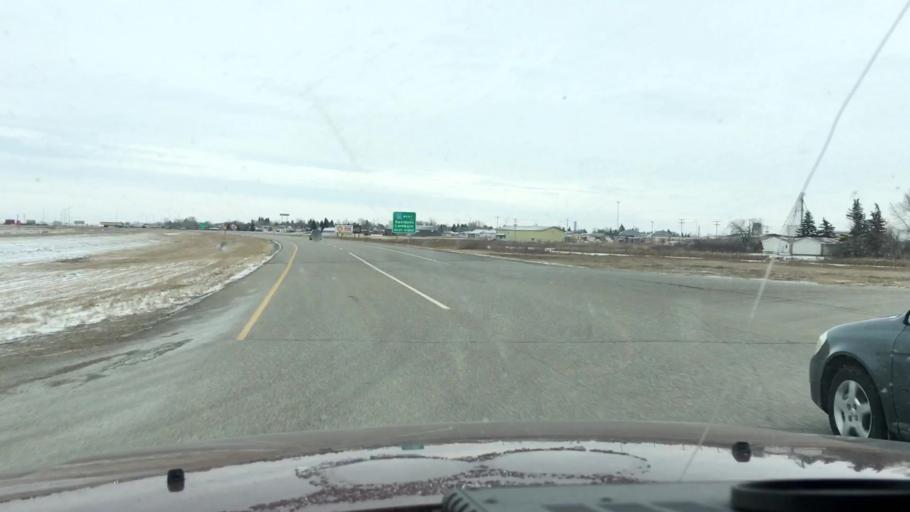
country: CA
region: Saskatchewan
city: Watrous
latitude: 51.2732
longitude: -106.0041
